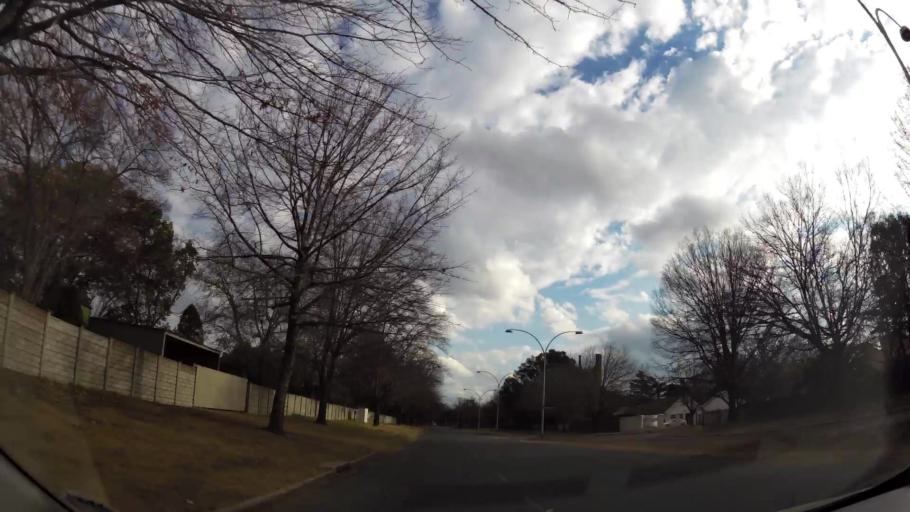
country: ZA
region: Orange Free State
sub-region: Fezile Dabi District Municipality
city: Sasolburg
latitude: -26.7979
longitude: 27.8216
